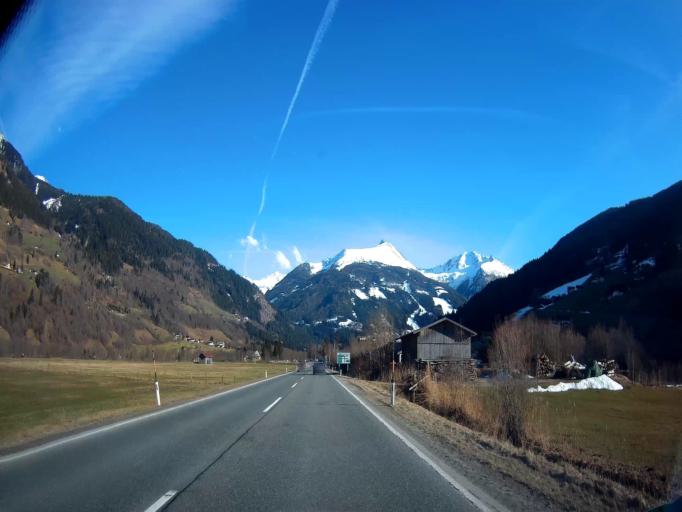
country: AT
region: Salzburg
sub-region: Politischer Bezirk Sankt Johann im Pongau
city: Bad Hofgastein
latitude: 47.1459
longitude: 13.1173
